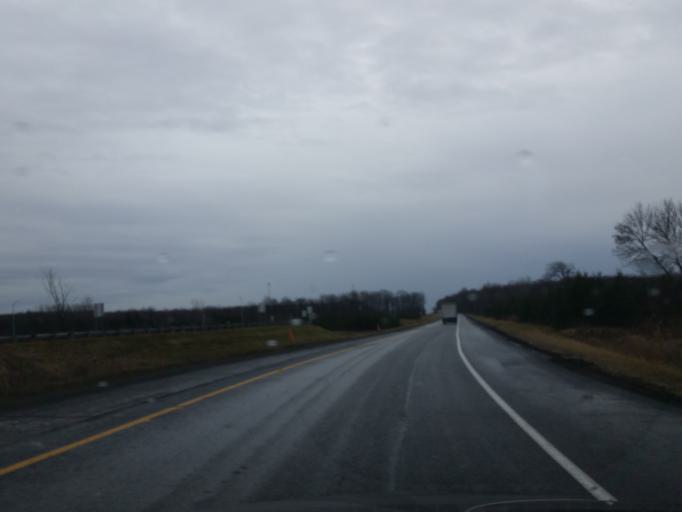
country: CA
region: Quebec
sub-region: Laurentides
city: Saint-Jerome
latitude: 45.7178
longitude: -73.9759
